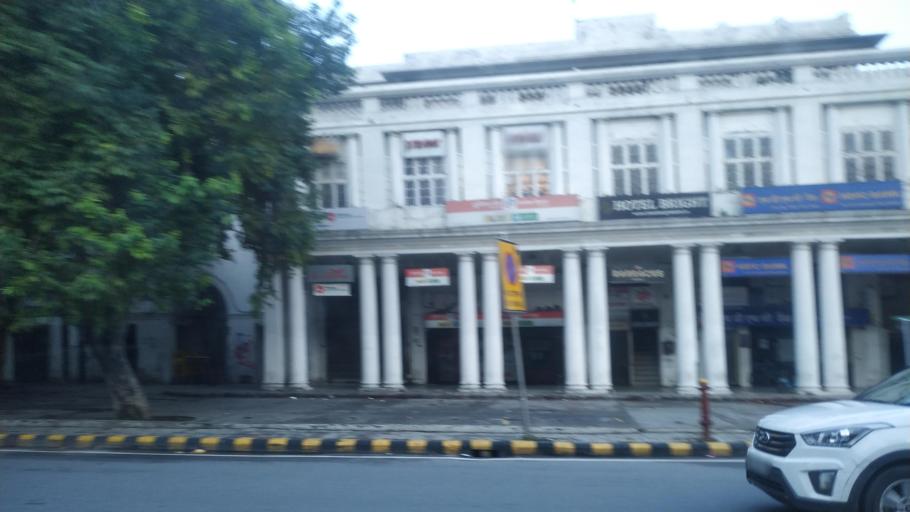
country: IN
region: NCT
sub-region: New Delhi
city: New Delhi
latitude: 28.6328
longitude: 77.2230
